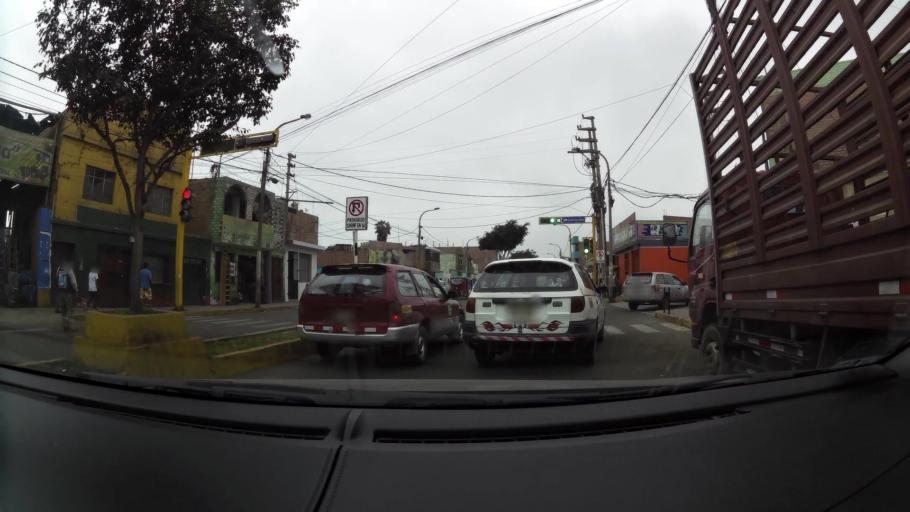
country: PE
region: Lima
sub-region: Provincia de Huaral
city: Chancay
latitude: -11.5643
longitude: -77.2685
